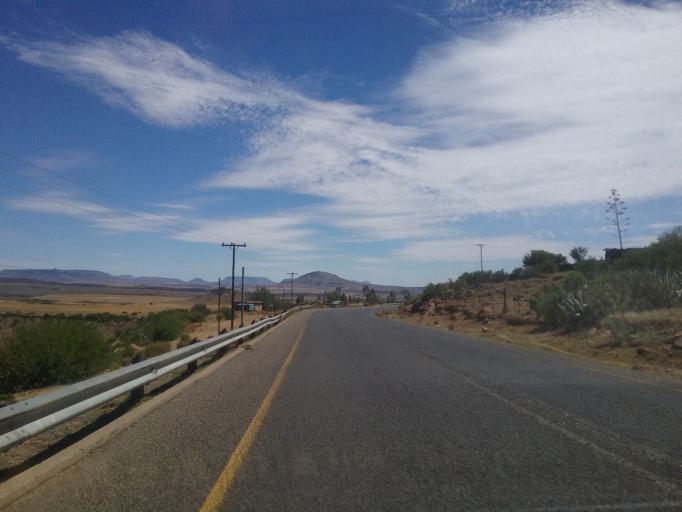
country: LS
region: Mohale's Hoek District
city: Mohale's Hoek
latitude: -30.1954
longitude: 27.4151
